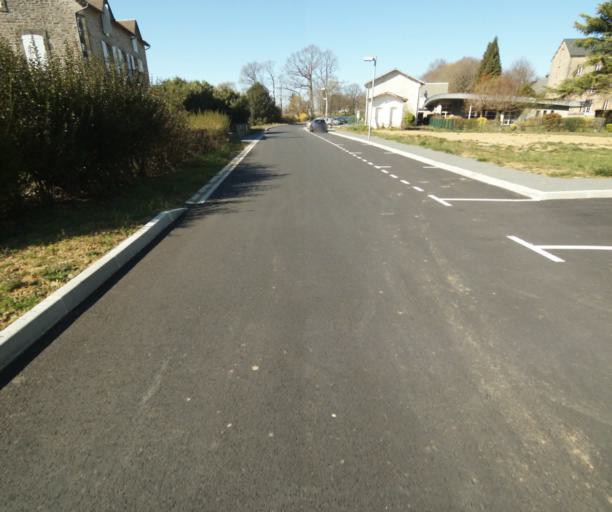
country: FR
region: Limousin
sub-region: Departement de la Correze
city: Chamboulive
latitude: 45.4677
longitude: 1.7392
